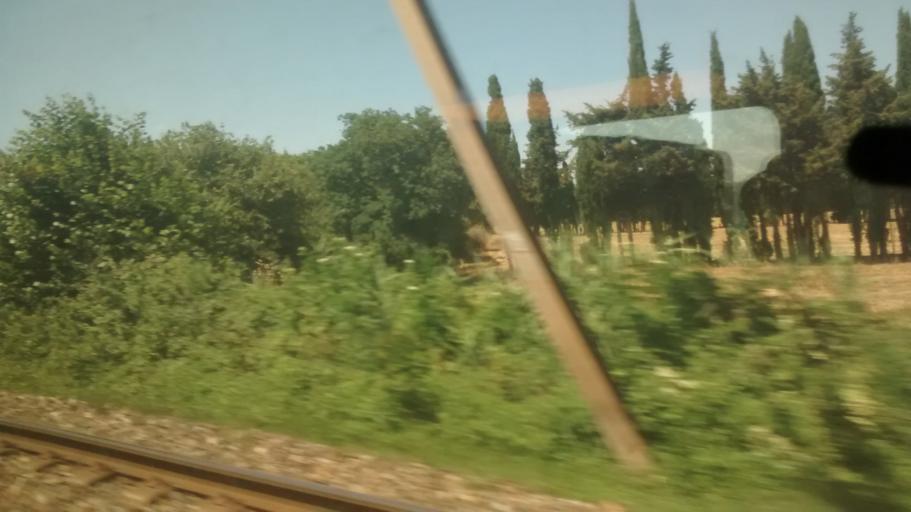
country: FR
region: Languedoc-Roussillon
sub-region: Departement du Gard
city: Rodilhan
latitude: 43.8388
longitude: 4.4369
